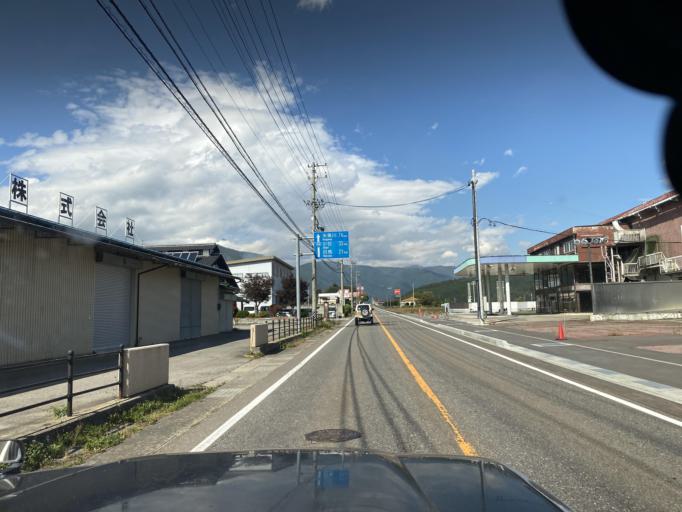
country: JP
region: Nagano
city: Omachi
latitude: 36.5281
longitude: 137.8492
